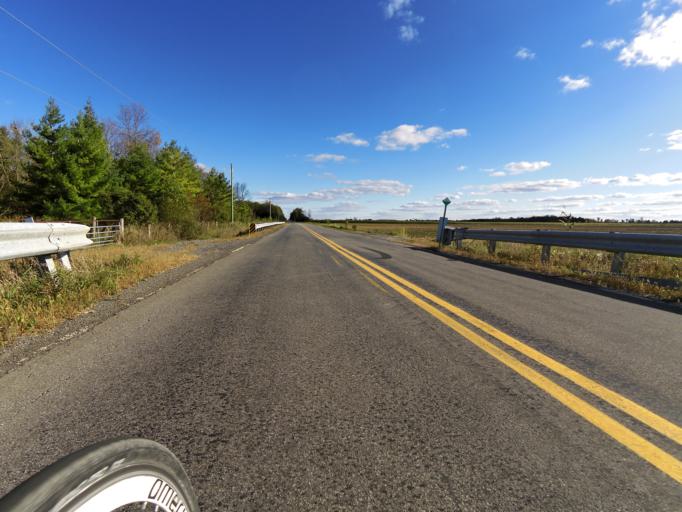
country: CA
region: Ontario
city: Bells Corners
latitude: 45.1348
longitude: -75.7545
